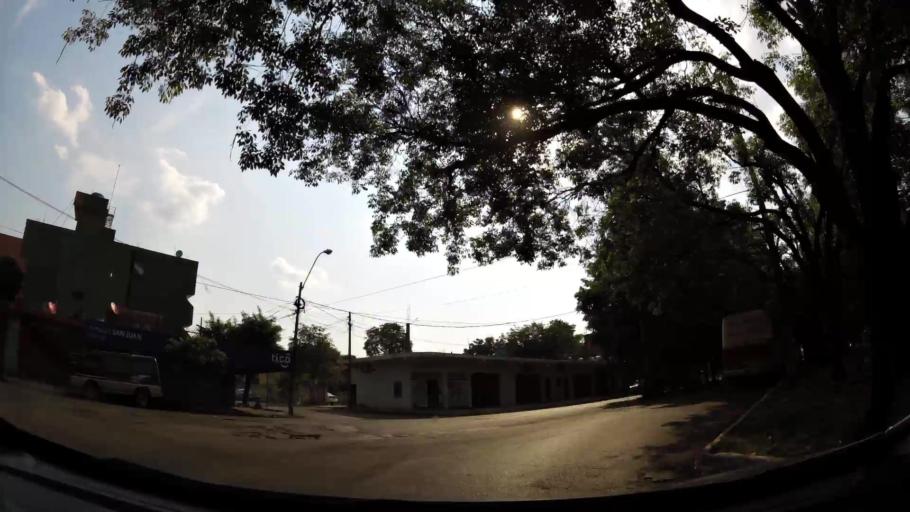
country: PY
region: Alto Parana
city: Presidente Franco
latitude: -25.5282
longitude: -54.6151
